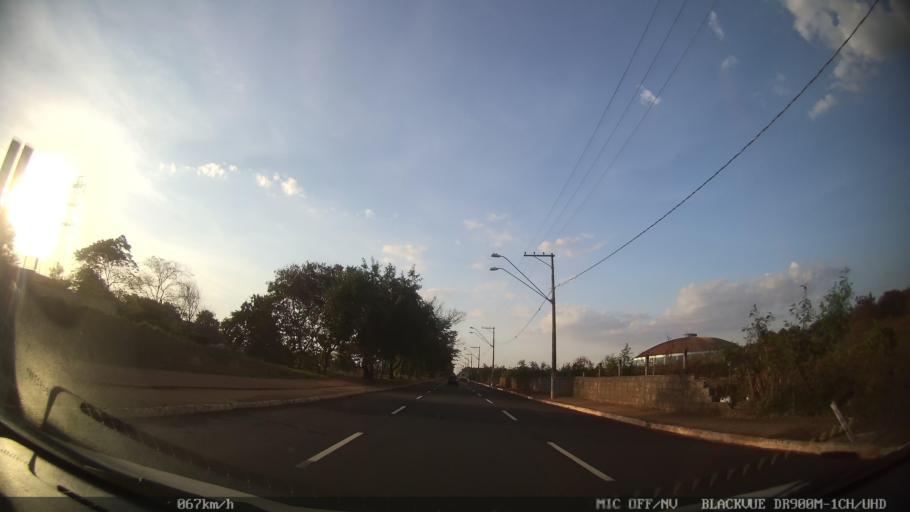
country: BR
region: Sao Paulo
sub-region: Ribeirao Preto
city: Ribeirao Preto
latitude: -21.1331
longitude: -47.8033
